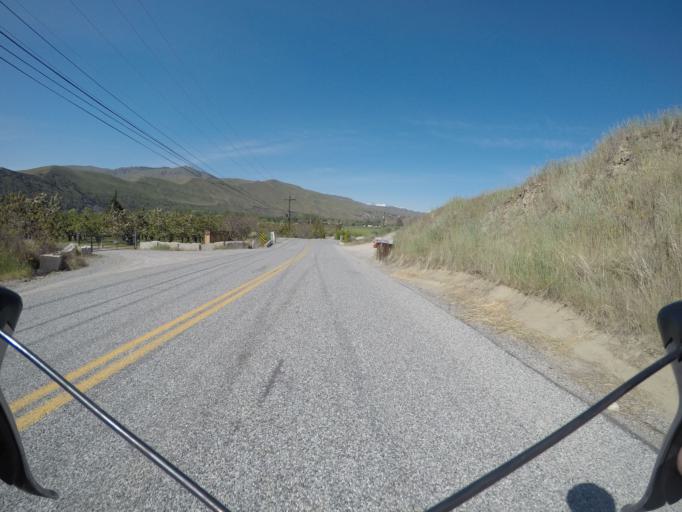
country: US
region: Washington
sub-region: Chelan County
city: Sunnyslope
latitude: 47.4694
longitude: -120.3500
